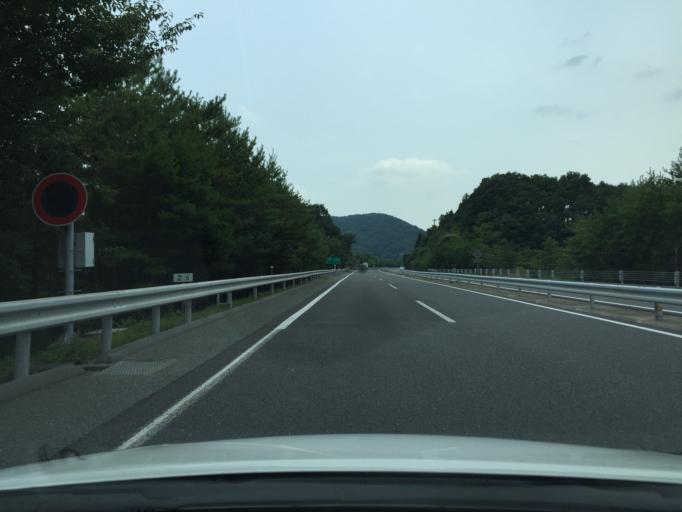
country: JP
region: Fukushima
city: Iwaki
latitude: 37.0559
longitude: 140.8009
